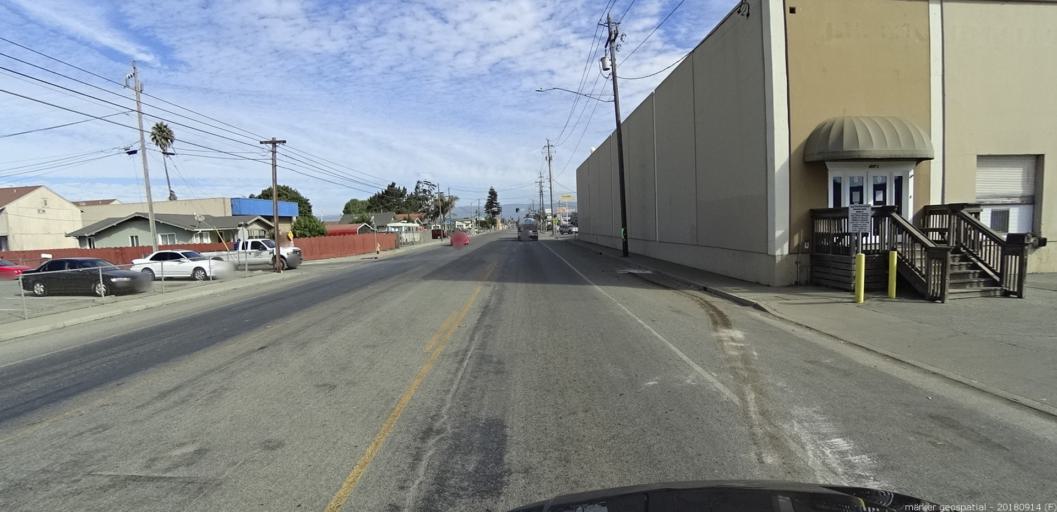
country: US
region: California
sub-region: Monterey County
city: Pajaro
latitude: 36.8974
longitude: -121.7479
